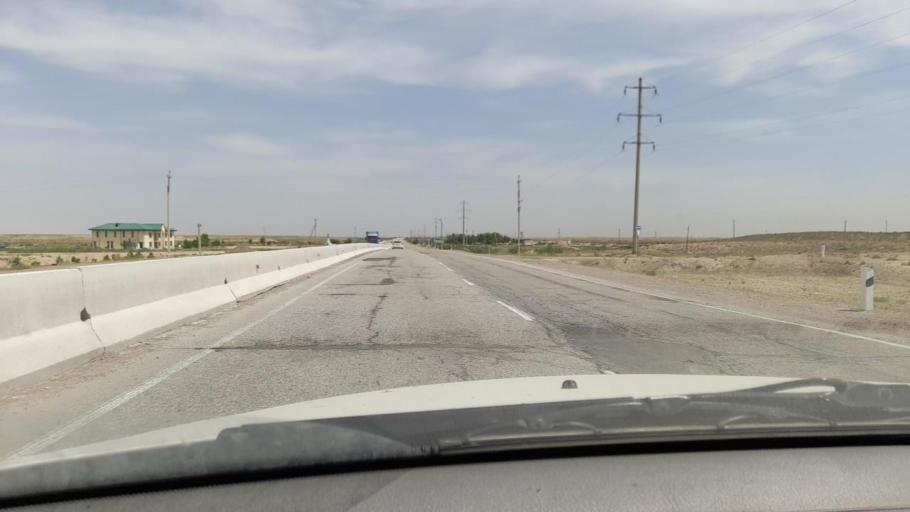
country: UZ
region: Navoiy
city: Qiziltepa
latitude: 40.0699
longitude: 64.9066
